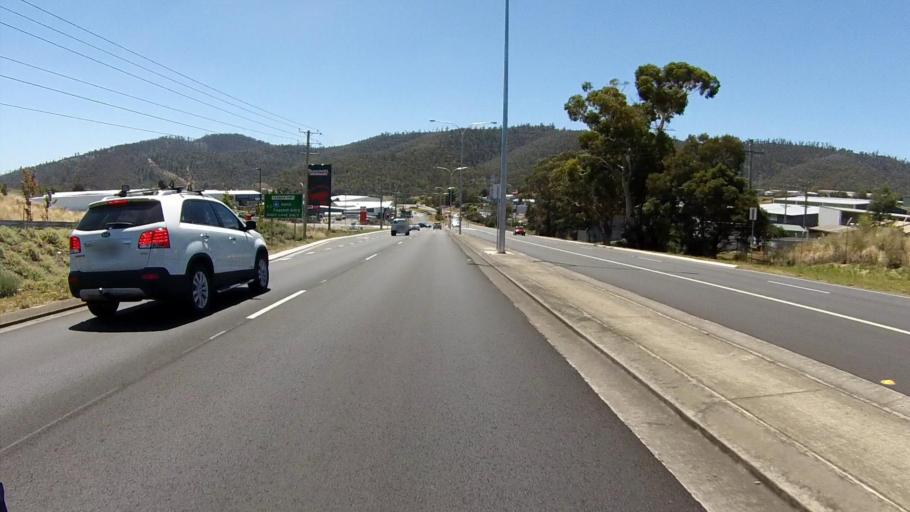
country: AU
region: Tasmania
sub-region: Clarence
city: Warrane
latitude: -42.8615
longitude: 147.3935
